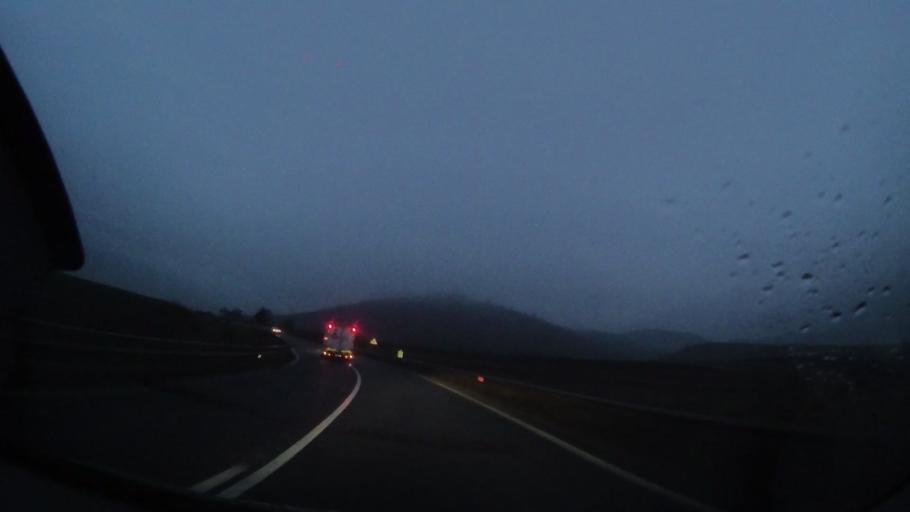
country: RO
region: Harghita
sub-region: Comuna Ditrau
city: Ditrau
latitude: 46.8368
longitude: 25.4895
